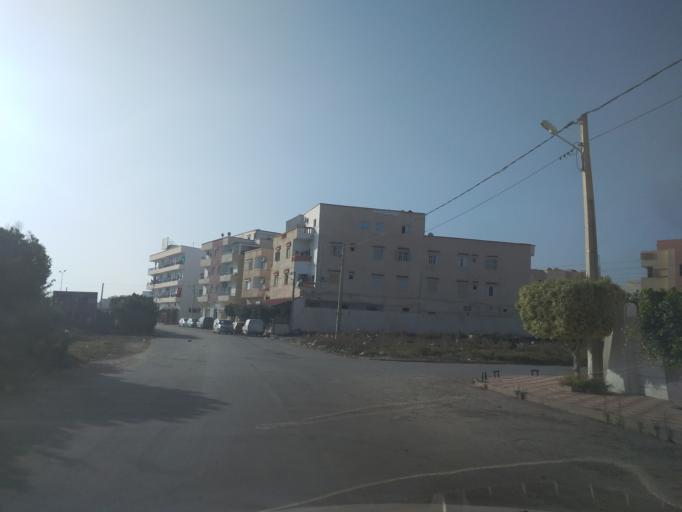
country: TN
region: Manouba
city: Manouba
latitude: 36.7893
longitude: 10.0841
